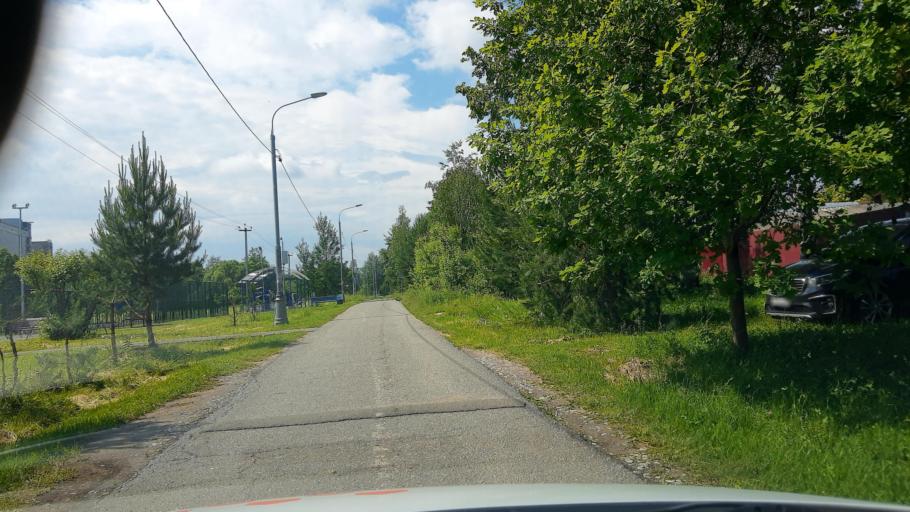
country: RU
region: Moskovskaya
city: Aprelevka
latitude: 55.2896
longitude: 37.1219
